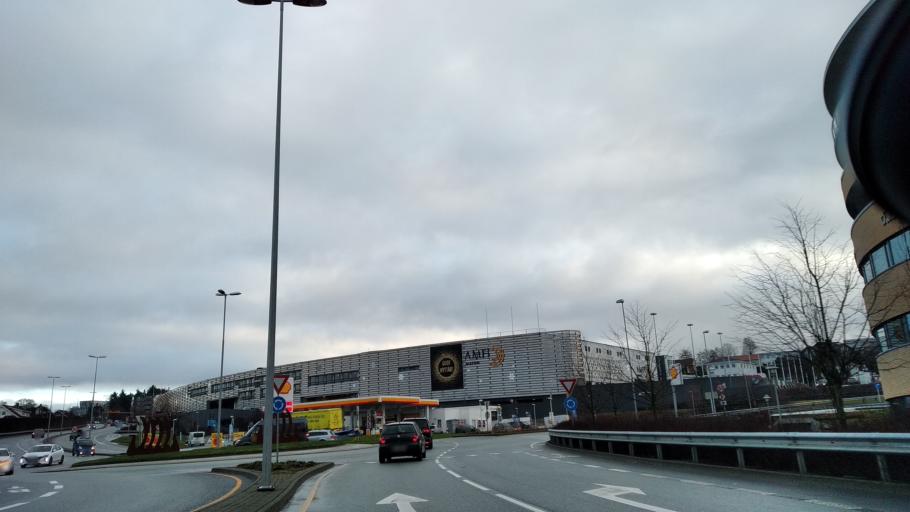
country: NO
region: Rogaland
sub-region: Stavanger
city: Stavanger
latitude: 58.9528
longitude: 5.6746
